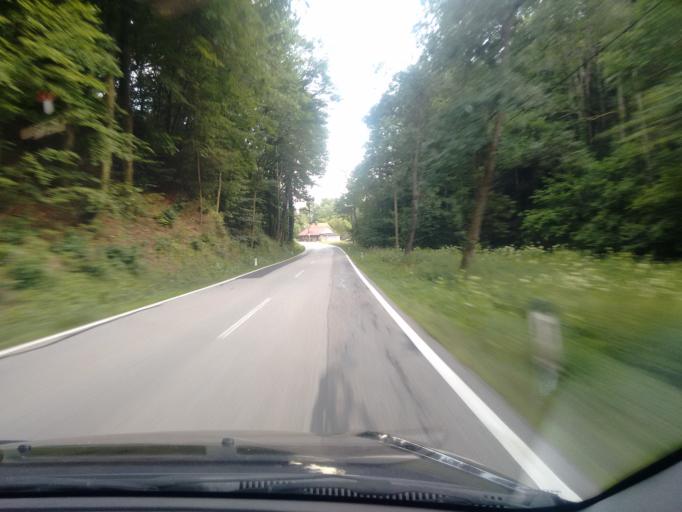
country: AT
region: Upper Austria
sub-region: Politischer Bezirk Urfahr-Umgebung
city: Feldkirchen an der Donau
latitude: 48.3774
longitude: 14.0634
